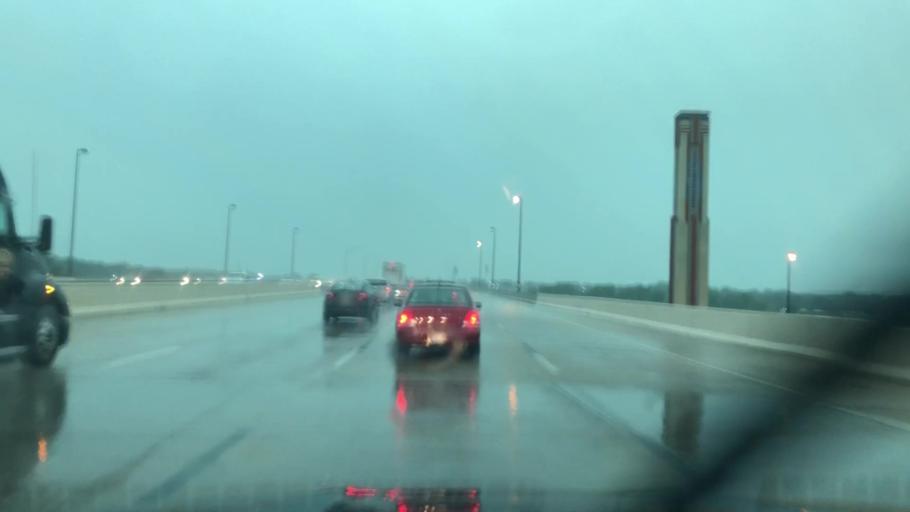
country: US
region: Oklahoma
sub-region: Tulsa County
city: Tulsa
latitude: 36.0900
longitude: -95.9840
